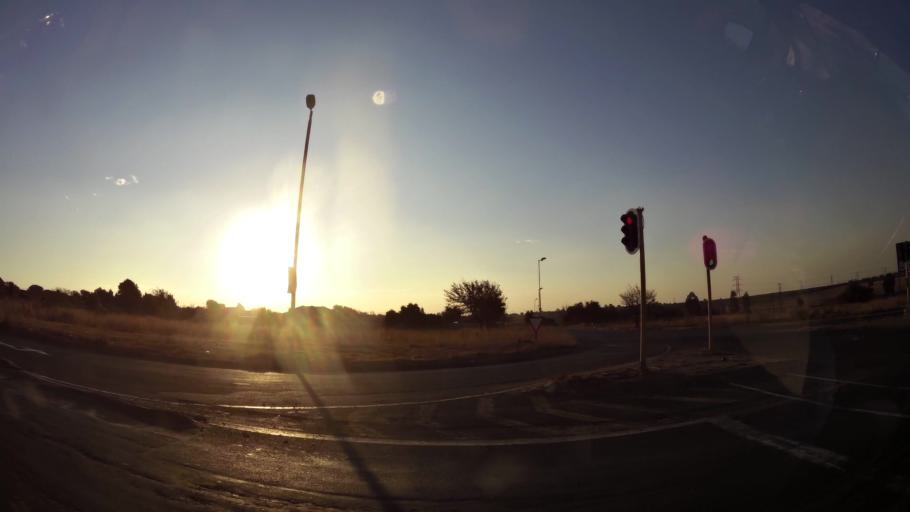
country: ZA
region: Gauteng
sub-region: West Rand District Municipality
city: Randfontein
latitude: -26.2063
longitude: 27.6608
